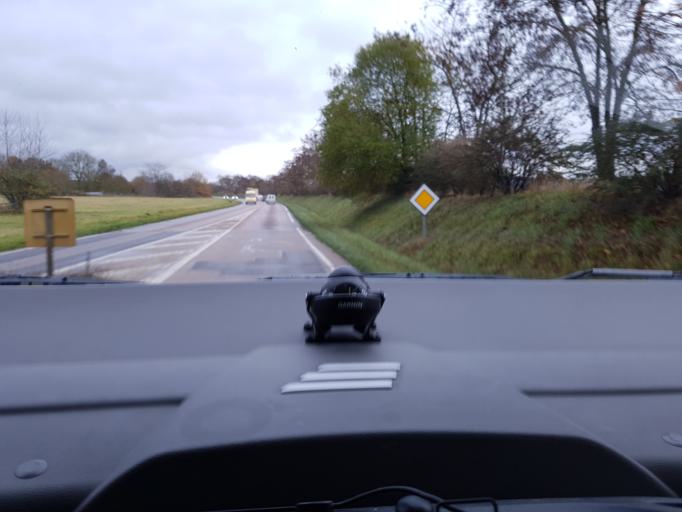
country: FR
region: Haute-Normandie
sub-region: Departement de l'Eure
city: Alizay
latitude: 49.3208
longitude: 1.1901
